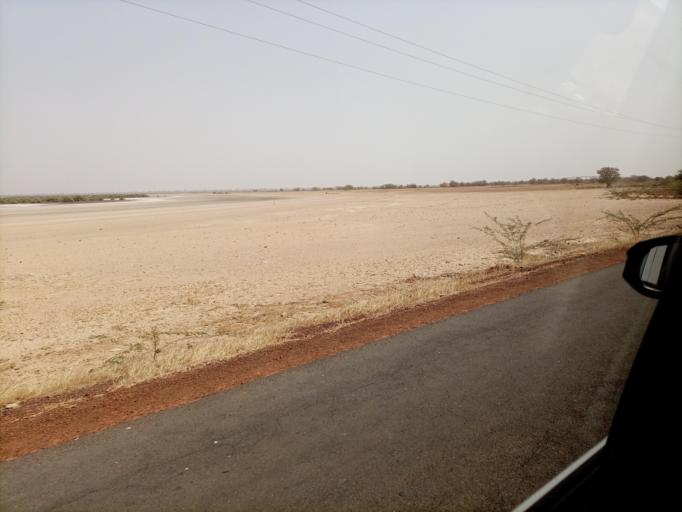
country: SN
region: Fatick
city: Foundiougne
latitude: 14.1658
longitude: -16.4639
